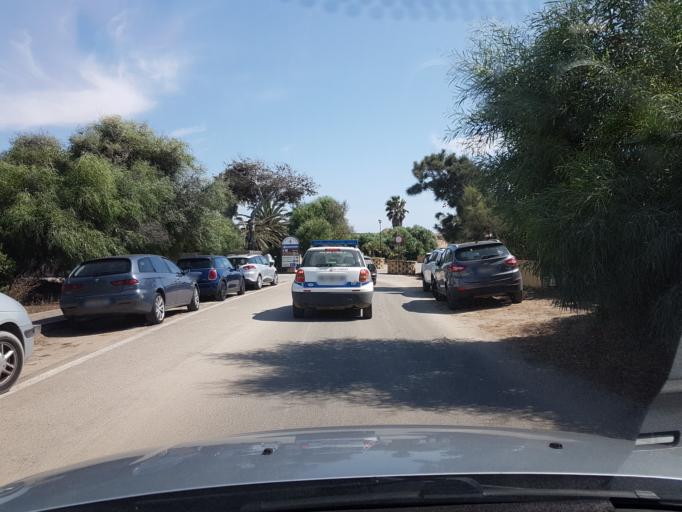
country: IT
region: Sardinia
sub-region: Provincia di Oristano
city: Cabras
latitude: 39.8836
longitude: 8.4383
